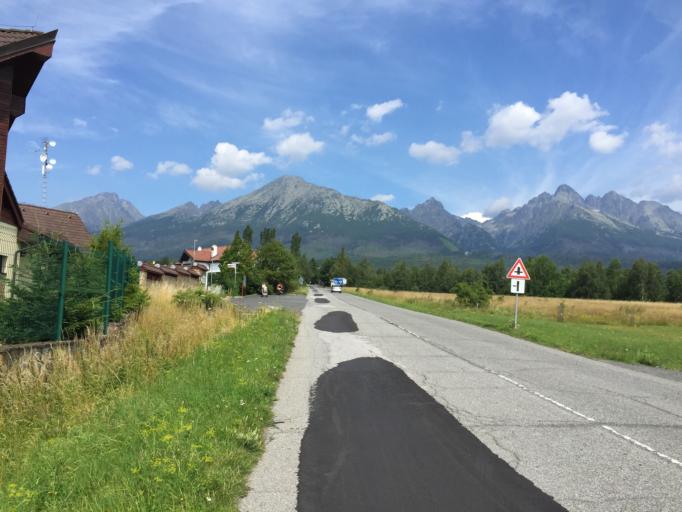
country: SK
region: Presovsky
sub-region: Okres Poprad
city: Nova Lesna
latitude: 49.1238
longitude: 20.2546
